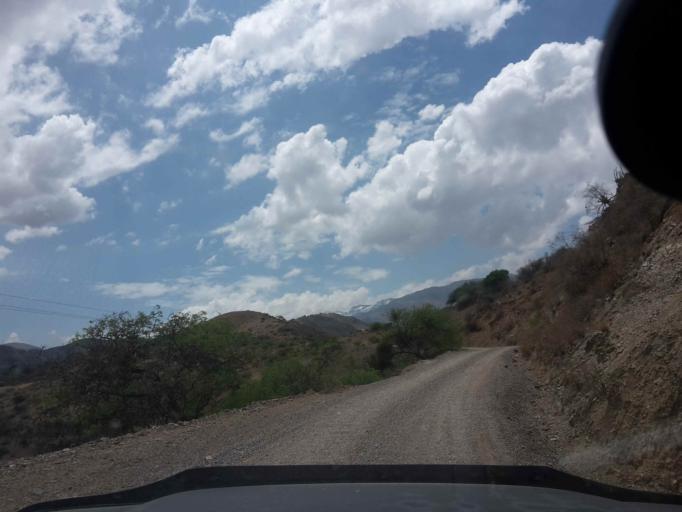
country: BO
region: Cochabamba
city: Sipe Sipe
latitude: -17.5459
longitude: -66.4789
